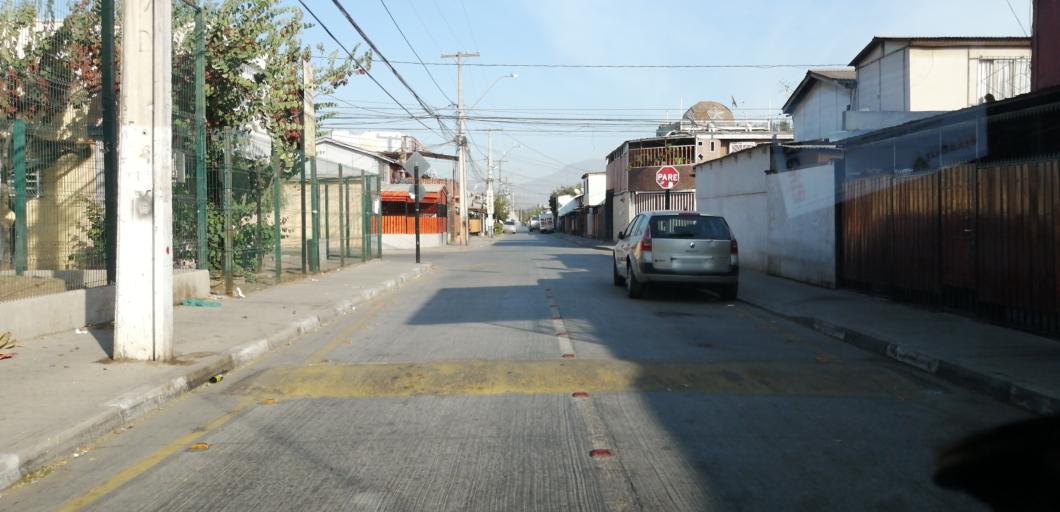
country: CL
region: Santiago Metropolitan
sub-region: Provincia de Santiago
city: Lo Prado
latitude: -33.4635
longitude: -70.7548
